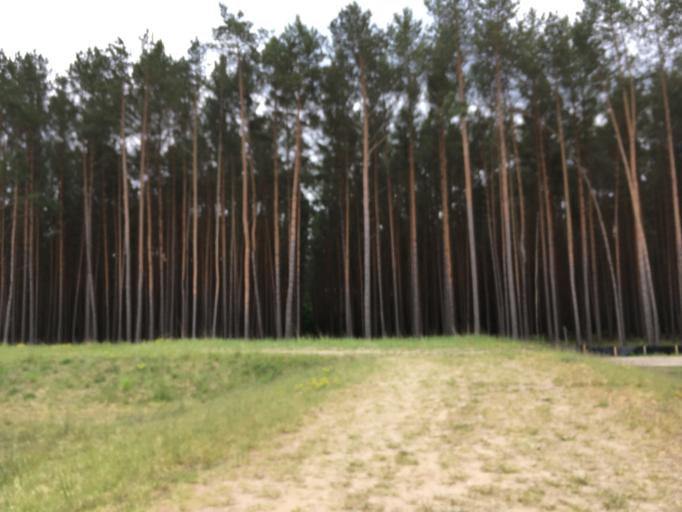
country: DE
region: Brandenburg
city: Marienwerder
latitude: 52.8546
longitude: 13.6442
